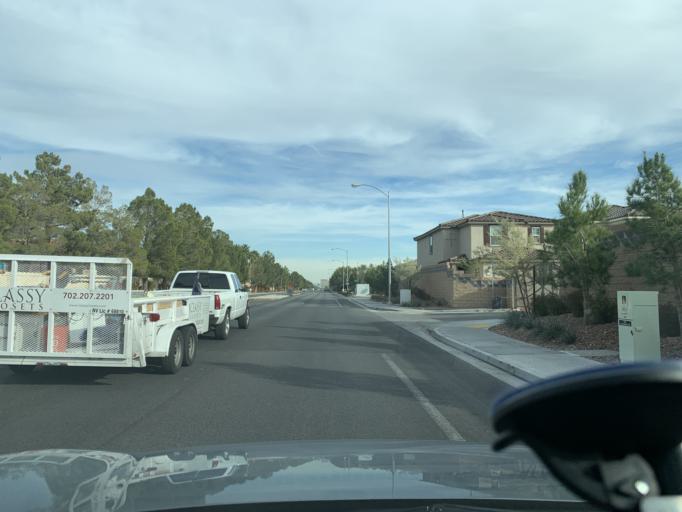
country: US
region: Nevada
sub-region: Clark County
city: Spring Valley
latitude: 36.0923
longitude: -115.2494
